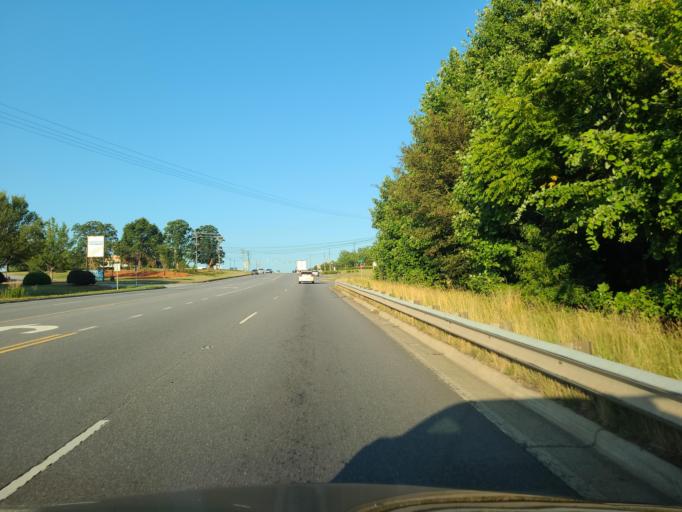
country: US
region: North Carolina
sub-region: Catawba County
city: Mountain View
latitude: 35.6925
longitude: -81.3558
